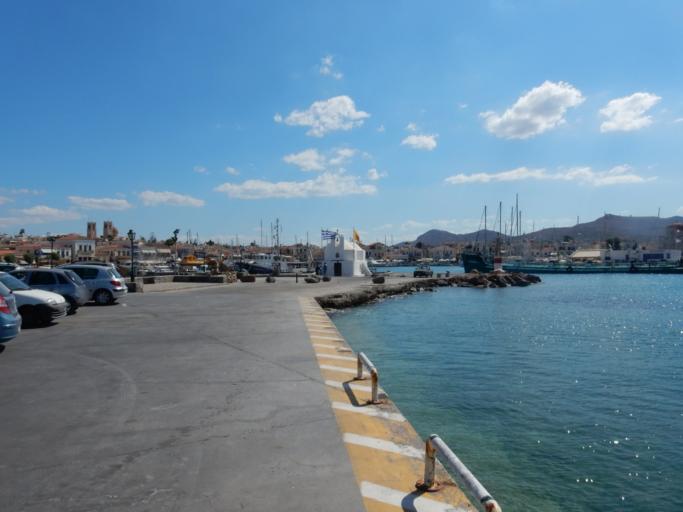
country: GR
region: Attica
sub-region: Nomos Piraios
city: Aegina
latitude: 37.7449
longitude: 23.4258
